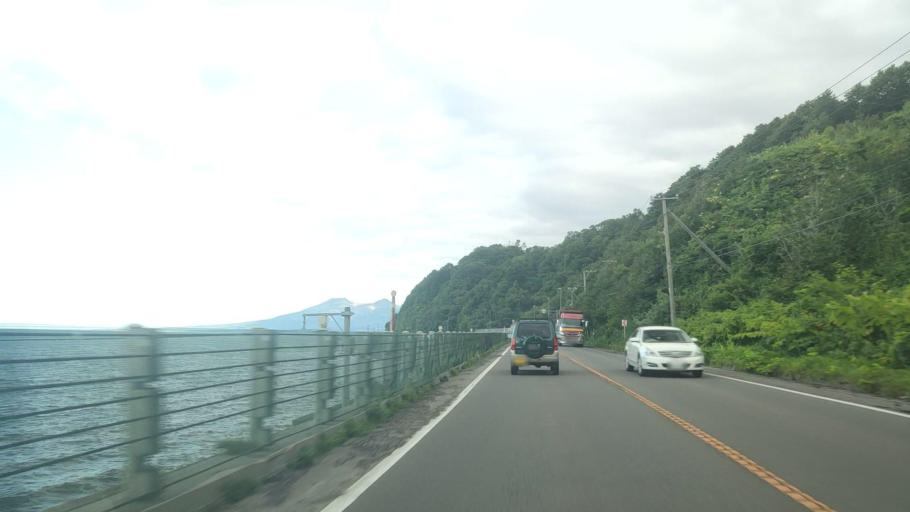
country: JP
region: Hokkaido
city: Nanae
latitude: 42.1658
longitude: 140.4630
